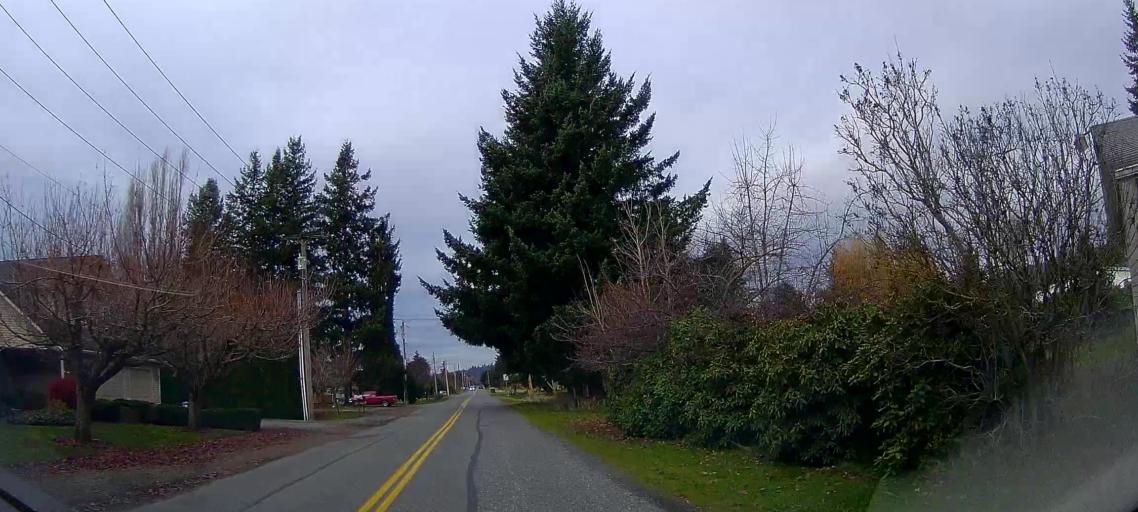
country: US
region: Washington
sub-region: Skagit County
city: Sedro-Woolley
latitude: 48.5112
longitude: -122.2481
